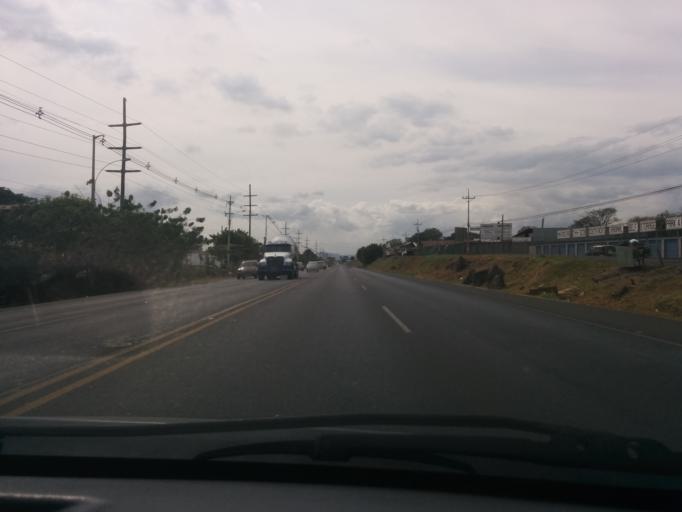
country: CR
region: Alajuela
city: Alajuela
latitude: 9.9944
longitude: -84.2370
